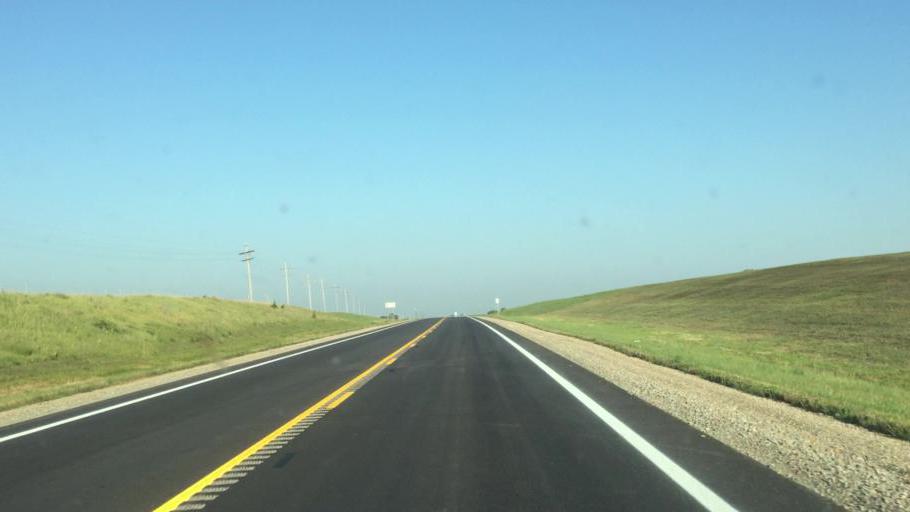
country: US
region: Kansas
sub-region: Brown County
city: Hiawatha
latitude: 39.8420
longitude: -95.4226
